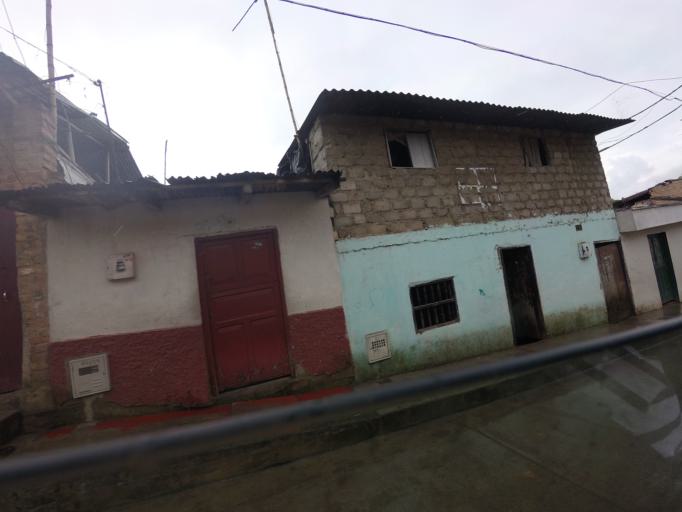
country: CO
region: Huila
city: Isnos
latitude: 1.9335
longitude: -76.2167
